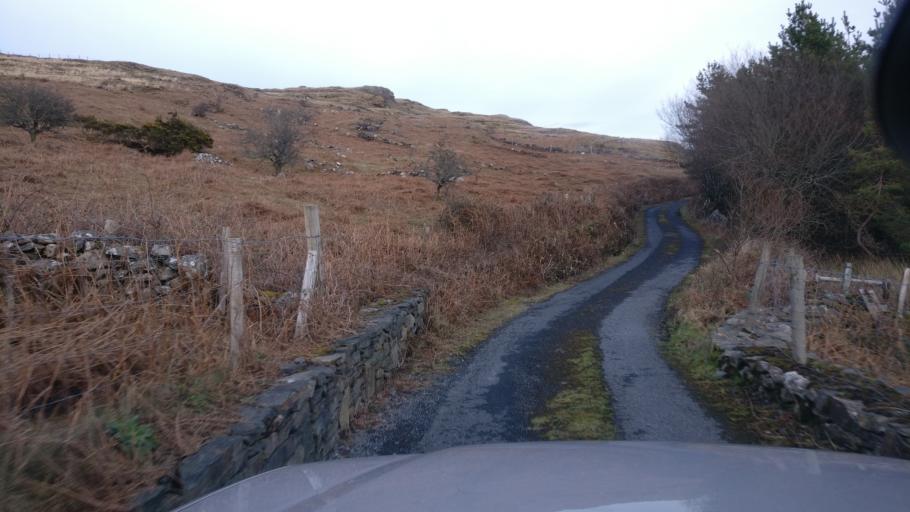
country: IE
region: Connaught
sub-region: County Galway
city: Oughterard
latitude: 53.5221
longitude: -9.4414
